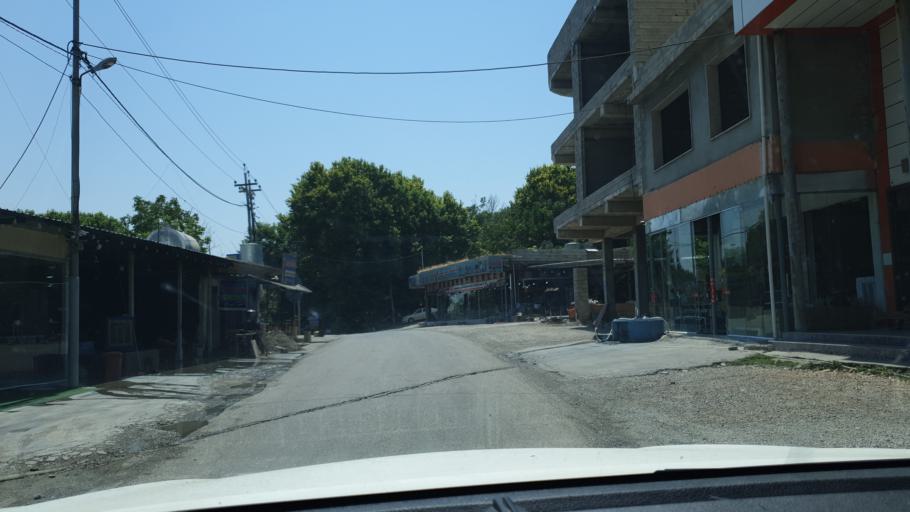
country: IQ
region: Arbil
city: Nahiyat Hiran
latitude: 36.2803
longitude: 44.4952
